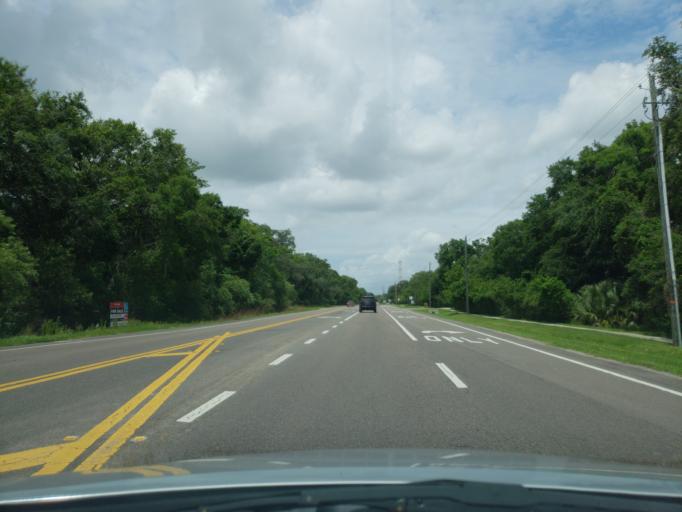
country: US
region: Florida
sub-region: Hillsborough County
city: East Lake-Orient Park
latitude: 28.0111
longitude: -82.3563
